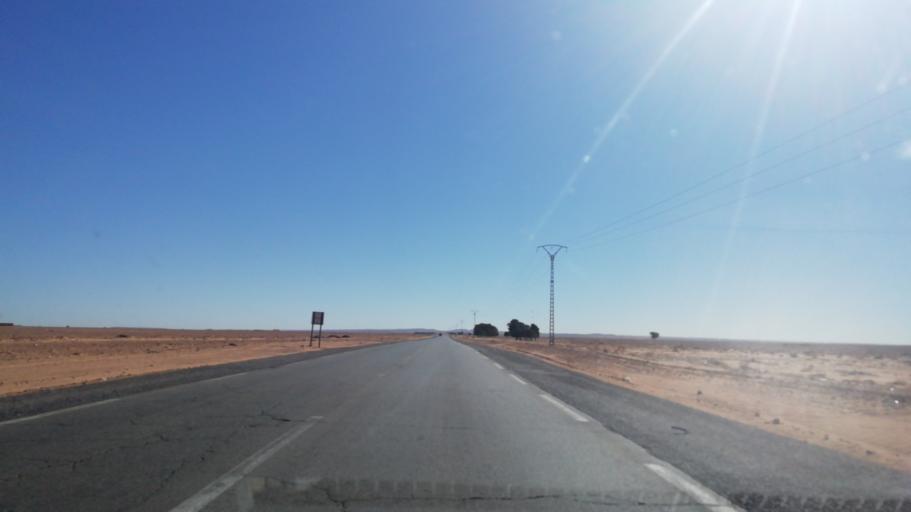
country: DZ
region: Saida
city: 'Ain el Hadjar
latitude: 34.0105
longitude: 0.1180
